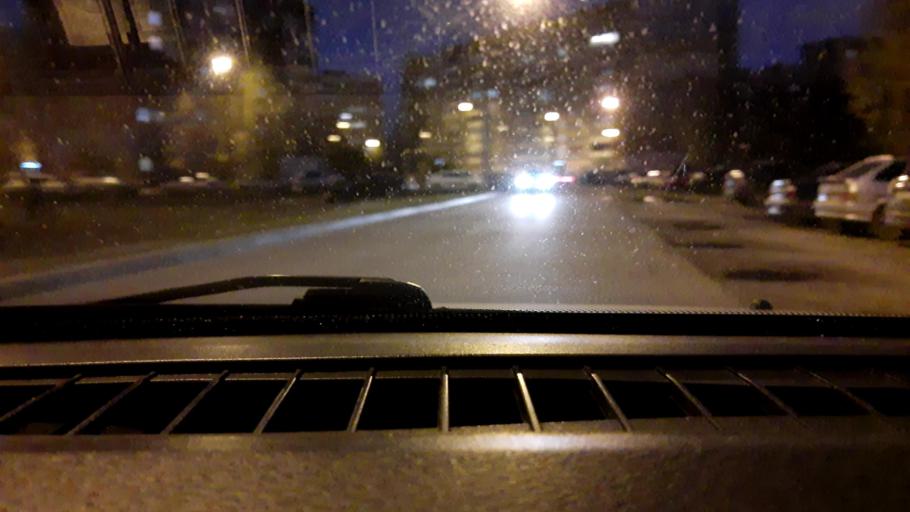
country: RU
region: Nizjnij Novgorod
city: Gorbatovka
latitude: 56.3683
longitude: 43.8002
